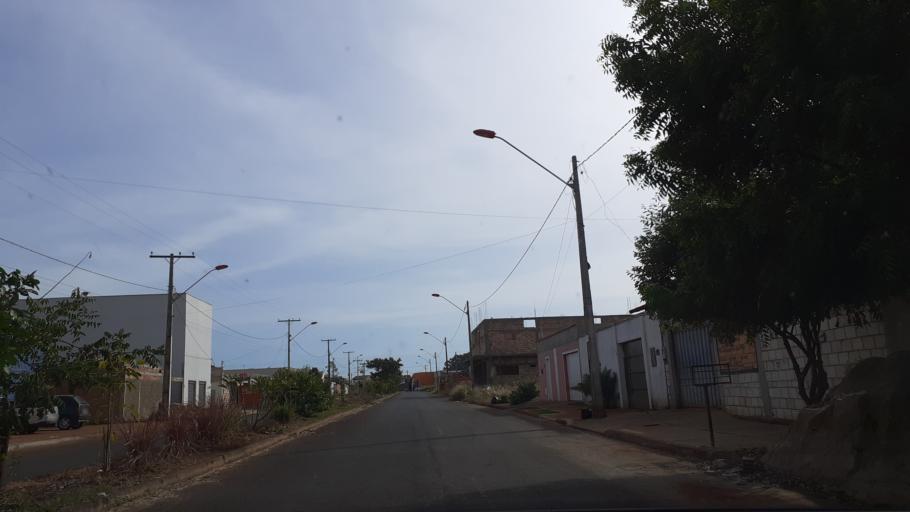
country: BR
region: Goias
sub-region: Itumbiara
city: Itumbiara
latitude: -18.4190
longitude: -49.2519
